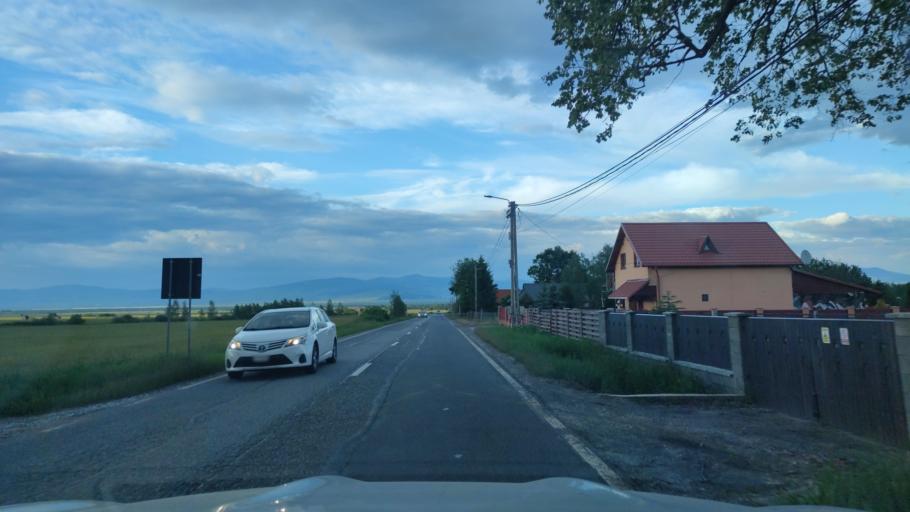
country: RO
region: Harghita
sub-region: Comuna Joseni
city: Joseni
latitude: 46.6846
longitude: 25.4106
